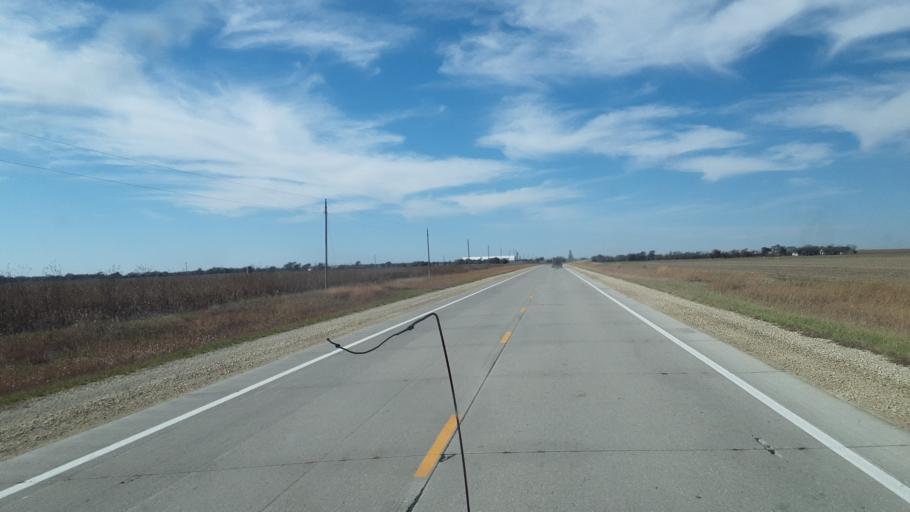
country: US
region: Kansas
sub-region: Marion County
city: Hillsboro
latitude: 38.3625
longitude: -97.1457
